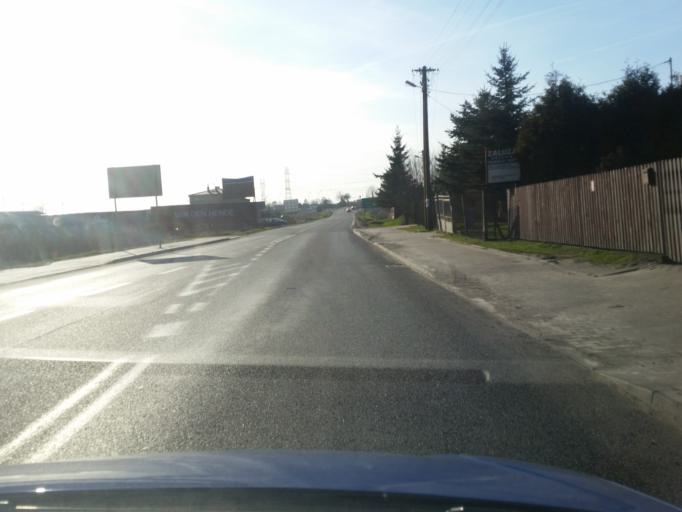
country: PL
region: Lodz Voivodeship
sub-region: Powiat radomszczanski
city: Radomsko
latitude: 51.0792
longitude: 19.3780
